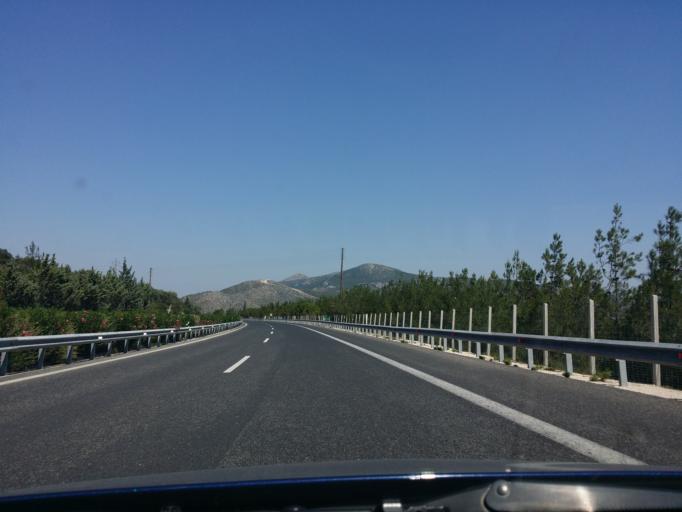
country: GR
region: Peloponnese
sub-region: Nomos Korinthias
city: Nemea
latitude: 37.7830
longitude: 22.6980
